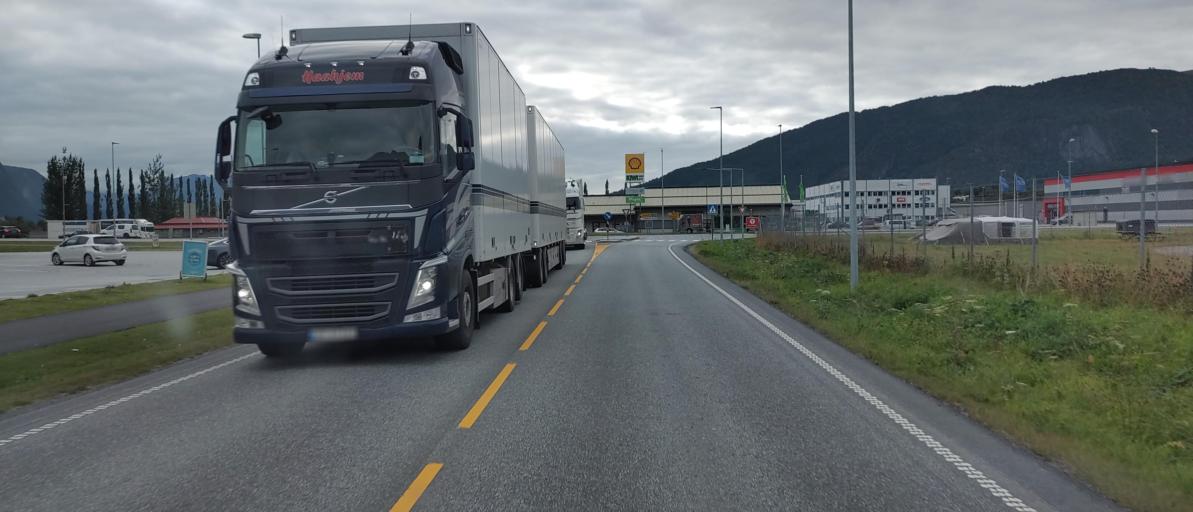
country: NO
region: More og Romsdal
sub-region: Rauma
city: Andalsnes
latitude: 62.5584
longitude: 7.6847
